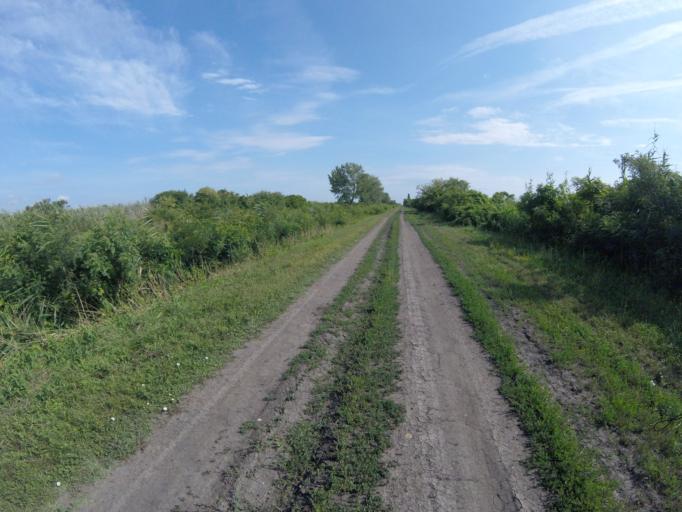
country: HU
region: Hajdu-Bihar
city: Hortobagy
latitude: 47.6309
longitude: 21.0811
